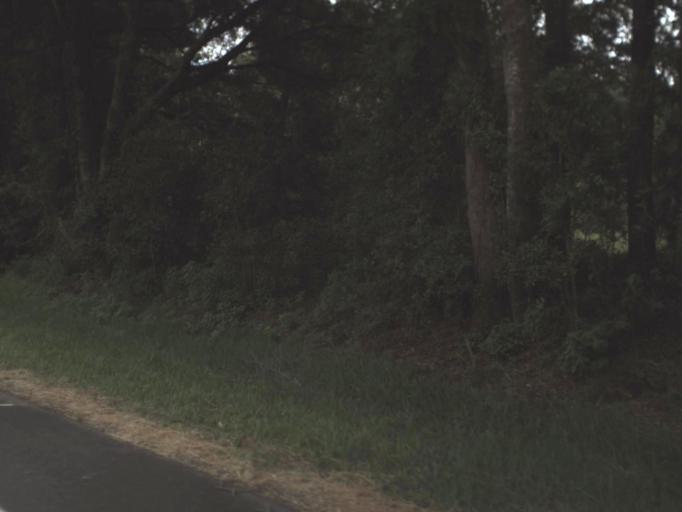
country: US
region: Florida
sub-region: Alachua County
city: Archer
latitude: 29.4992
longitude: -82.4968
